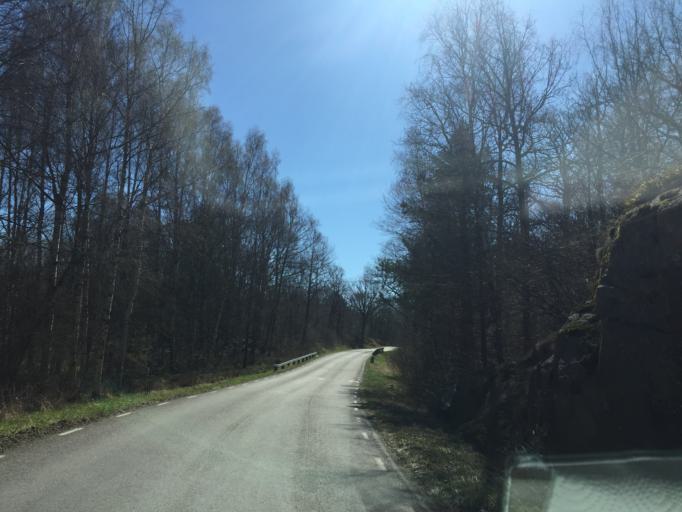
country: SE
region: Kalmar
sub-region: Oskarshamns Kommun
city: Oskarshamn
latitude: 57.2405
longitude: 16.4760
